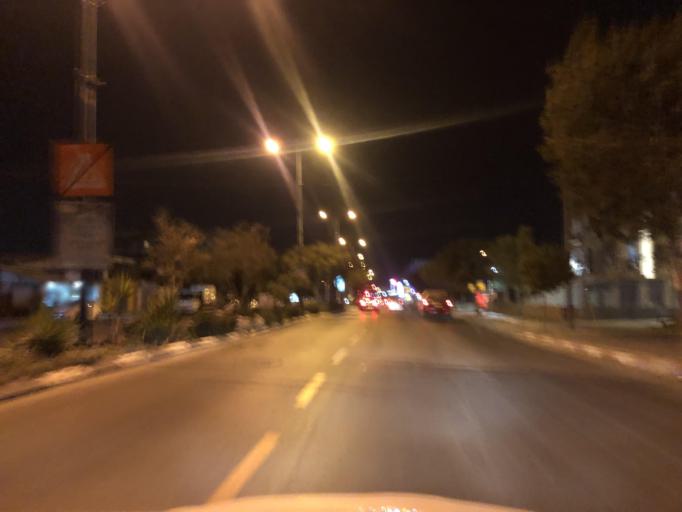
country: IL
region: Tel Aviv
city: Yafo
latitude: 32.0493
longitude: 34.7737
